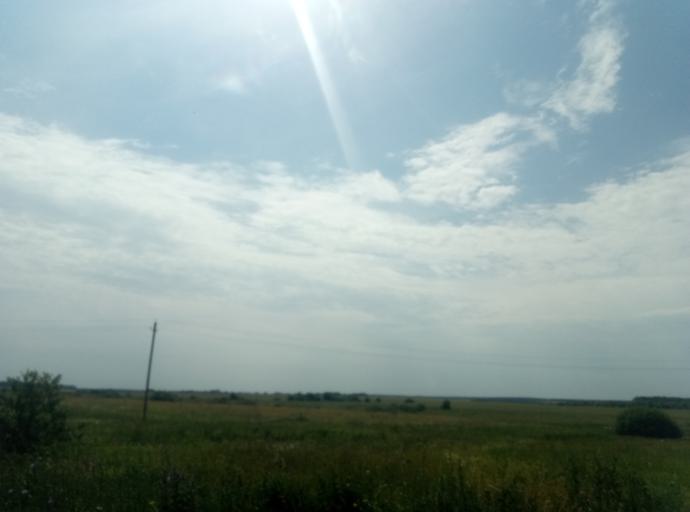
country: RU
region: Tula
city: Dubovka
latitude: 53.9001
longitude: 38.0063
